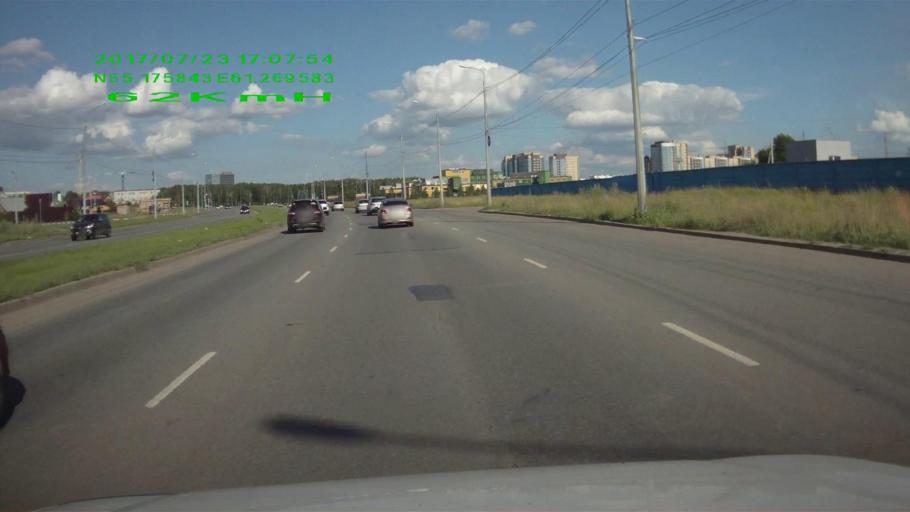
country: RU
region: Chelyabinsk
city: Roshchino
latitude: 55.1758
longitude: 61.2702
